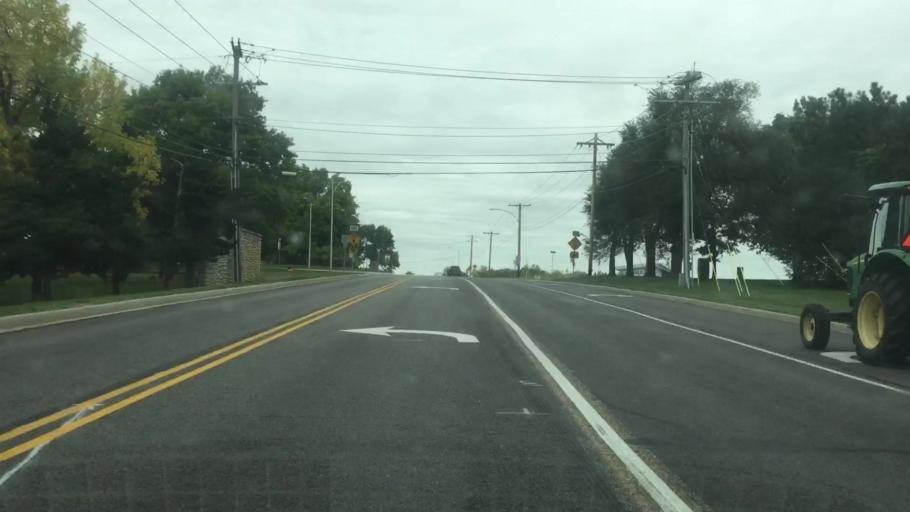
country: US
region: Kansas
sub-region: Johnson County
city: Lenexa
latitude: 38.9848
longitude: -94.7797
